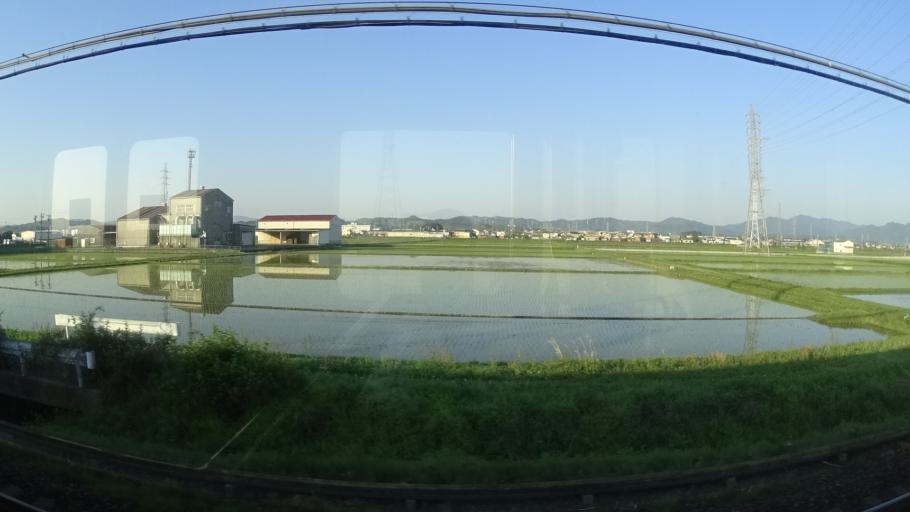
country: JP
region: Mie
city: Hisai-motomachi
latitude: 34.5615
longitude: 136.5542
